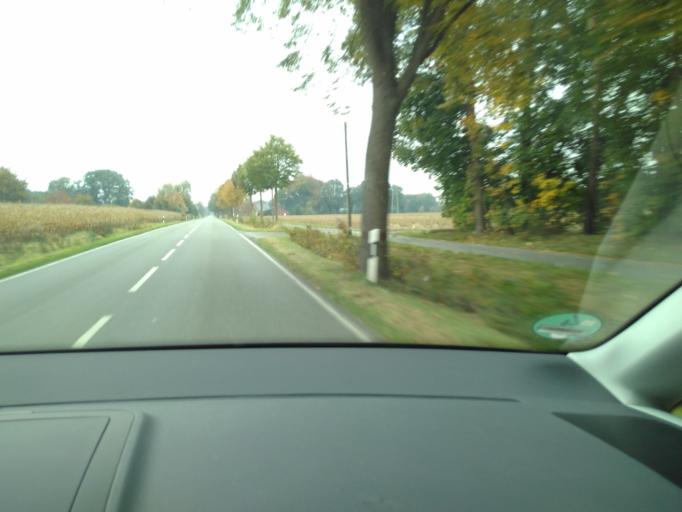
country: DE
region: North Rhine-Westphalia
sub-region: Regierungsbezirk Detmold
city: Verl
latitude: 51.9095
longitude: 8.5613
